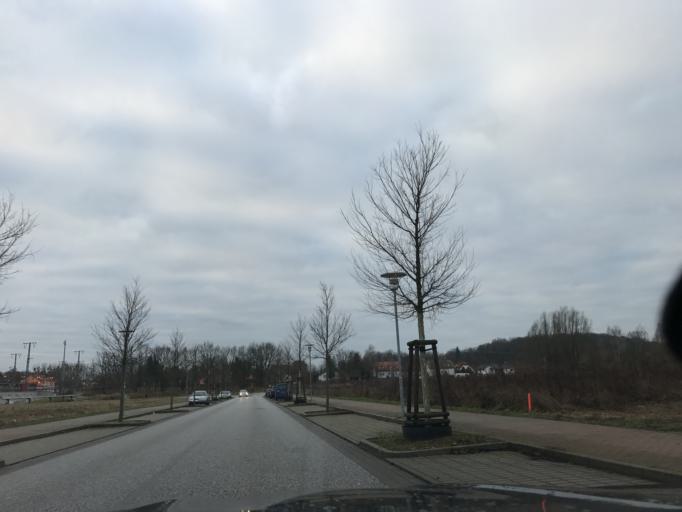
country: DE
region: Brandenburg
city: Werder
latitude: 52.4123
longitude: 12.9712
